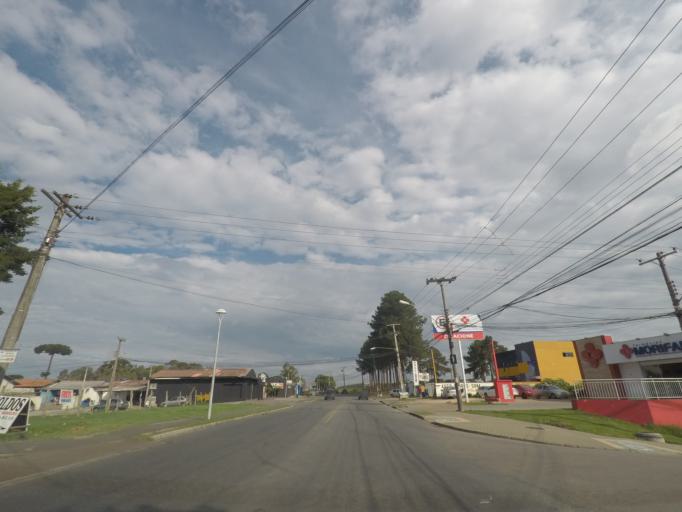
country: BR
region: Parana
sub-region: Sao Jose Dos Pinhais
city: Sao Jose dos Pinhais
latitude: -25.5420
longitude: -49.2946
